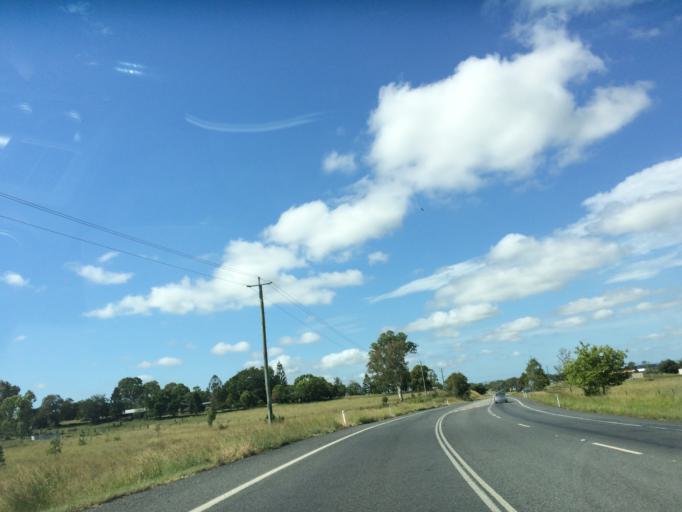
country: AU
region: Queensland
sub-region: Logan
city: Cedar Vale
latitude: -27.9126
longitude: 152.9847
